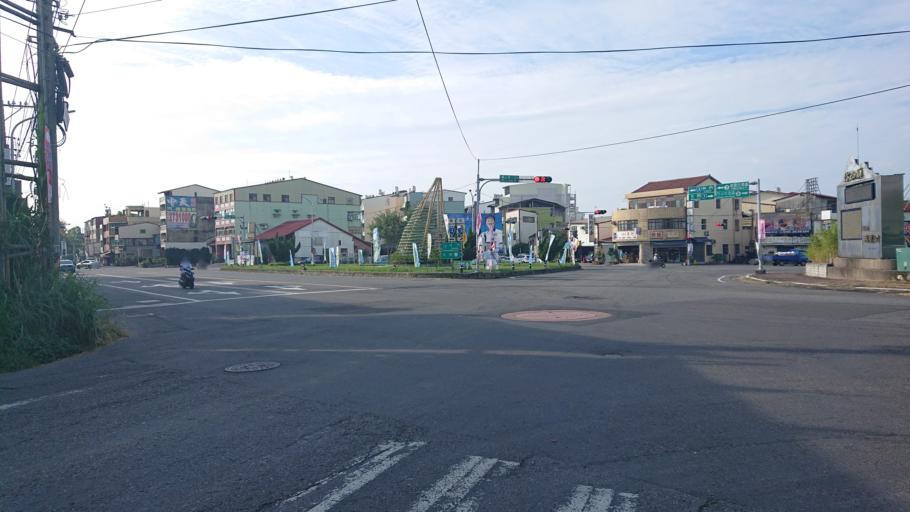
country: TW
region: Taiwan
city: Lugu
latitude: 23.7540
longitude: 120.6776
